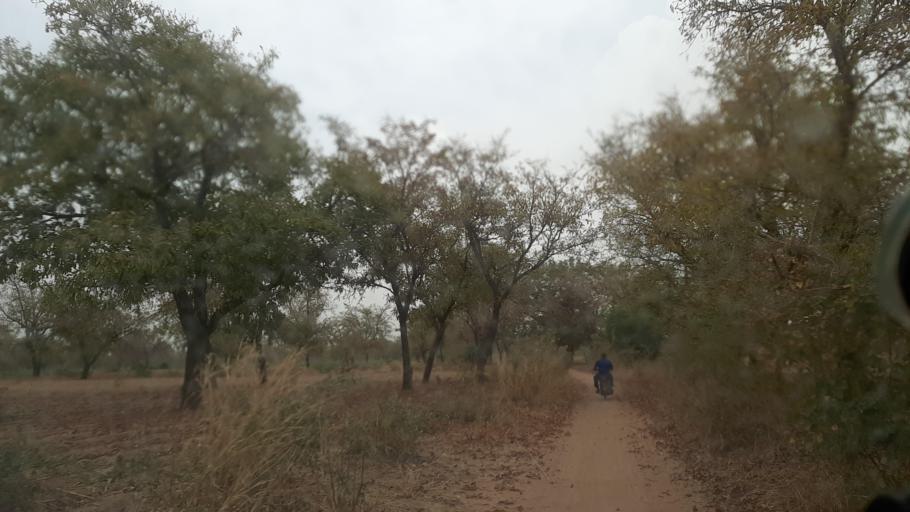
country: BF
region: Boucle du Mouhoun
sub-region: Province des Banwa
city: Salanso
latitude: 11.8562
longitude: -4.4308
